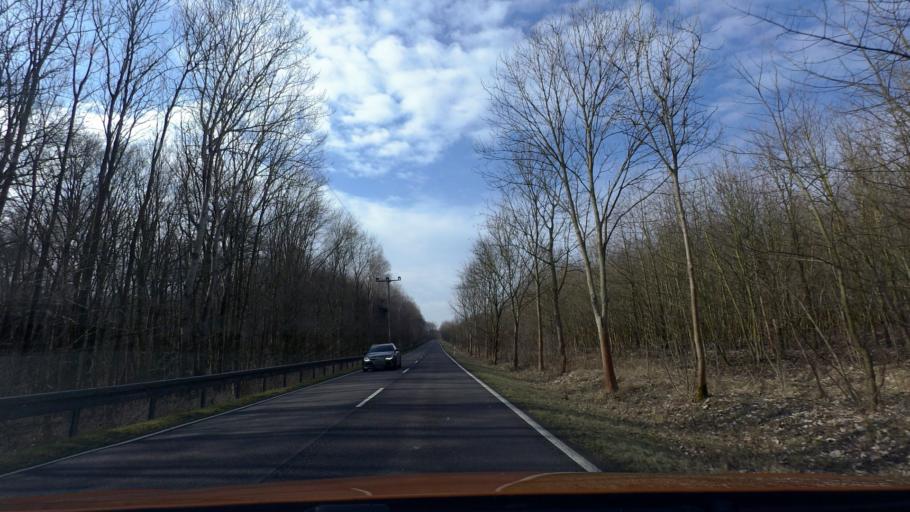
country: DE
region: Saxony-Anhalt
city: Beendorf
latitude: 52.2197
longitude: 11.0888
